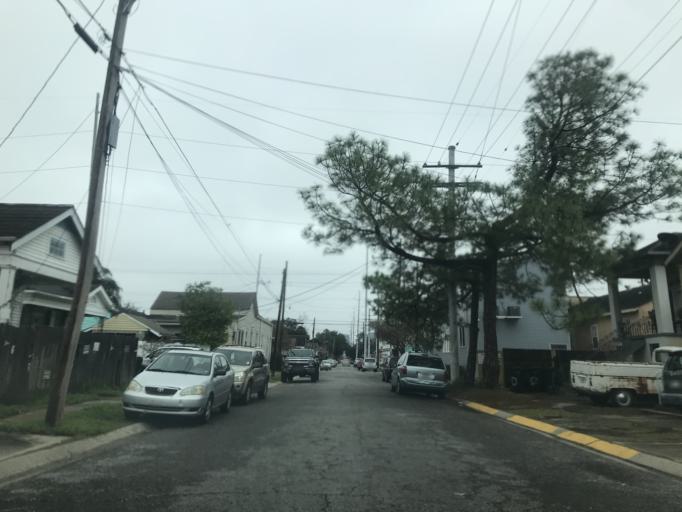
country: US
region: Louisiana
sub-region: Orleans Parish
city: New Orleans
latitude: 29.9688
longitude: -90.1005
